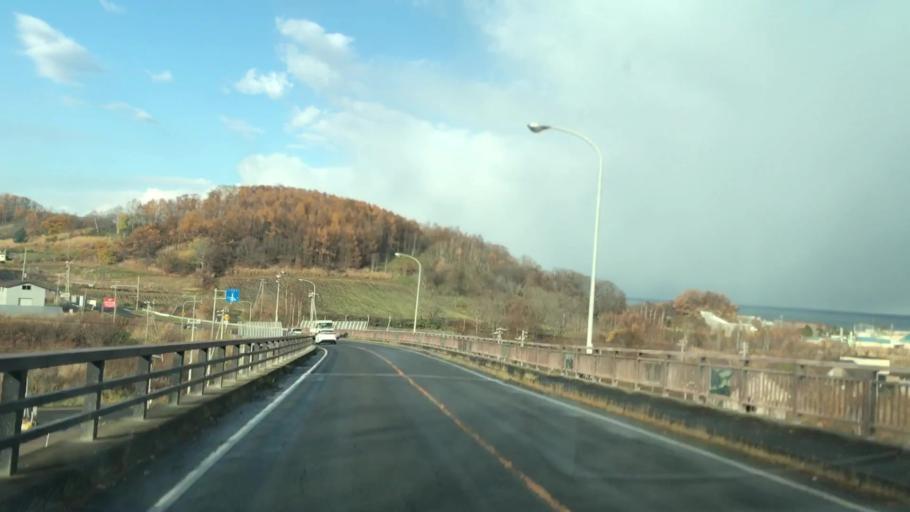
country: JP
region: Hokkaido
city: Yoichi
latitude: 43.1907
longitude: 140.8428
